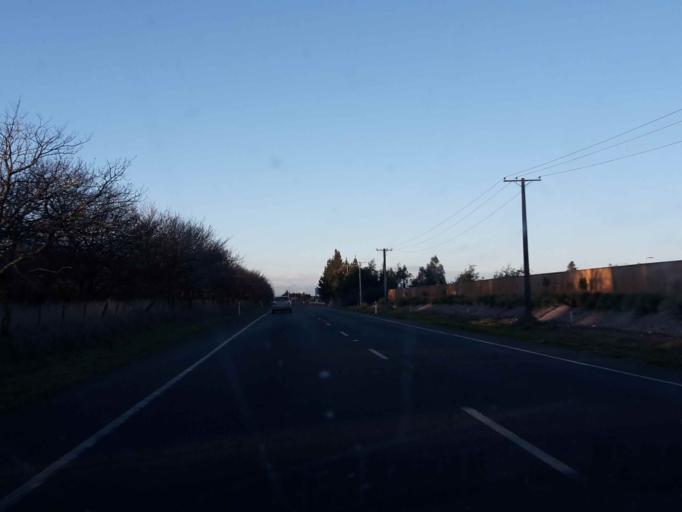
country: NZ
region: Canterbury
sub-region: Selwyn District
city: Rolleston
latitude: -43.5991
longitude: 172.3572
